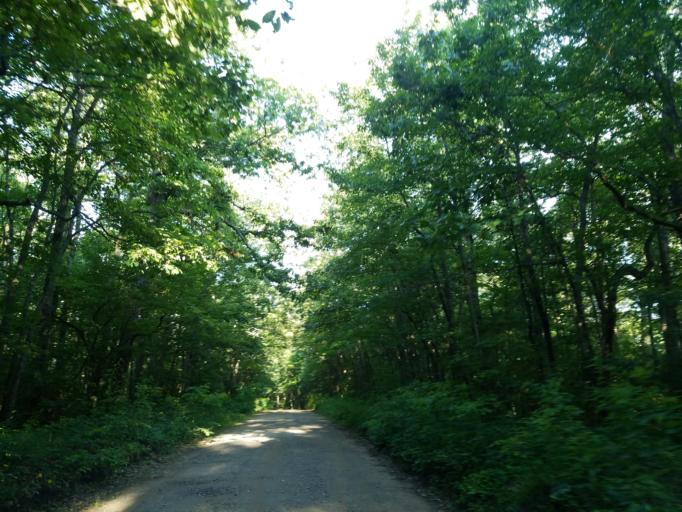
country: US
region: Georgia
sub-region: Lumpkin County
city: Dahlonega
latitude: 34.6585
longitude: -84.1171
